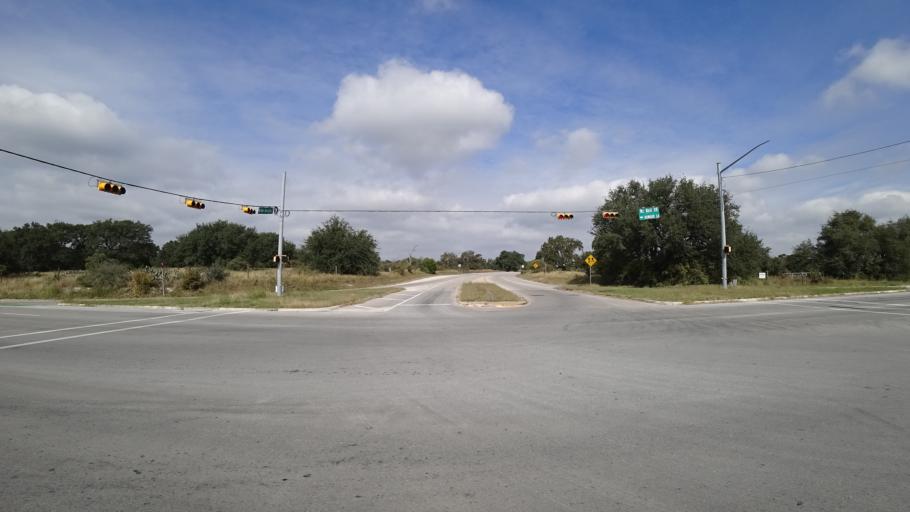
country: US
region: Texas
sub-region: Travis County
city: Wells Branch
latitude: 30.4489
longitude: -97.7258
